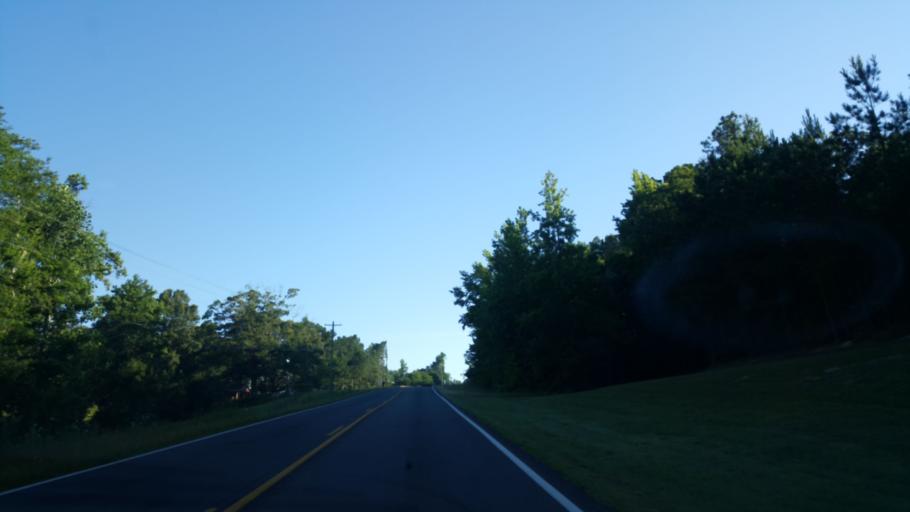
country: US
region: Tennessee
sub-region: Henderson County
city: Lexington
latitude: 35.5862
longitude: -88.3899
